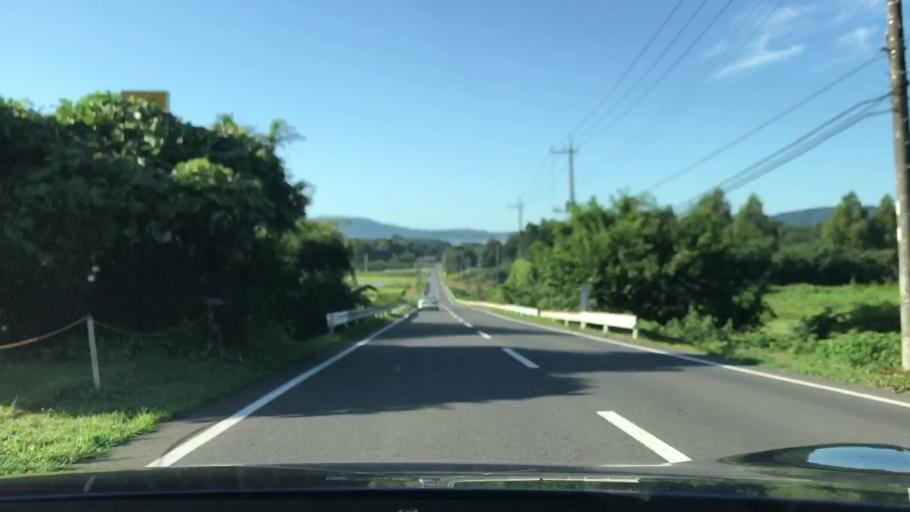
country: JP
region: Ibaraki
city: Makabe
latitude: 36.2492
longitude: 140.1648
